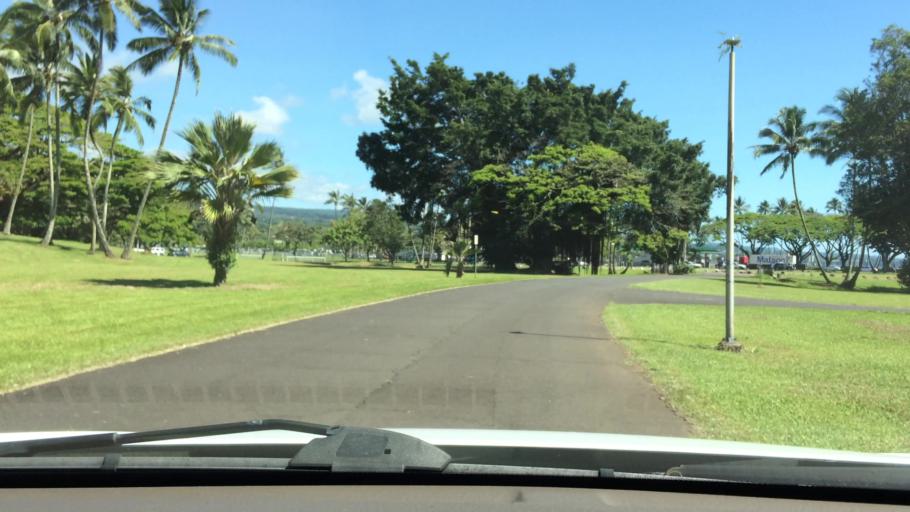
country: US
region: Hawaii
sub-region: Hawaii County
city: Hilo
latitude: 19.7199
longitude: -155.0776
